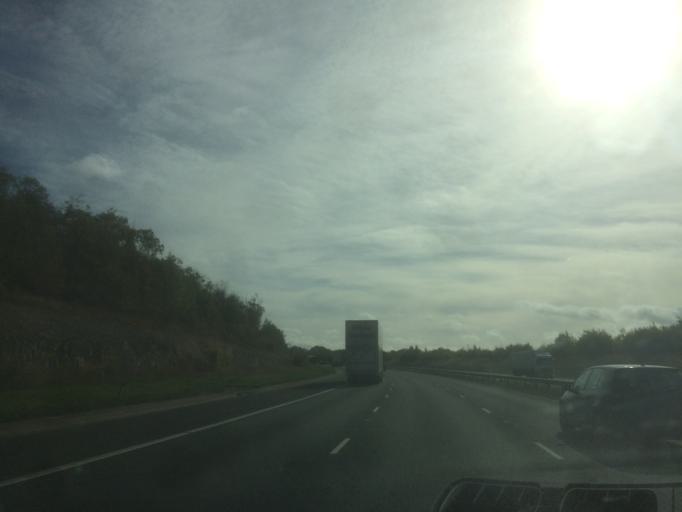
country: GB
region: England
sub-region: City and Borough of Leeds
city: Ledsham
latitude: 53.7831
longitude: -1.3192
